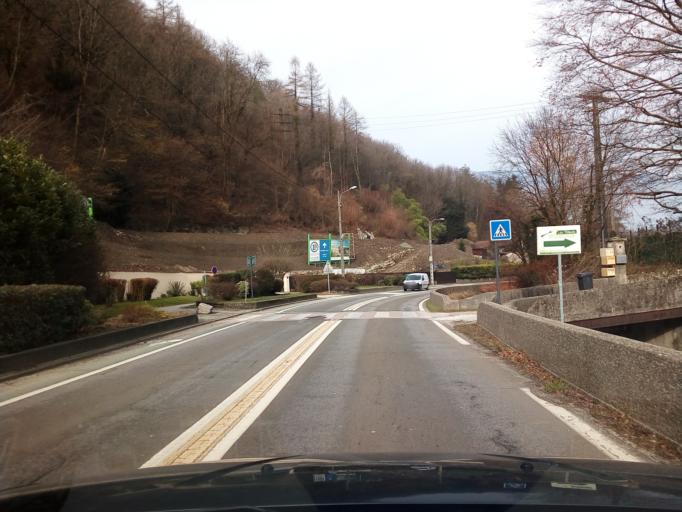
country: FR
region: Rhone-Alpes
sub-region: Departement de l'Isere
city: Gieres
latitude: 45.1756
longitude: 5.7898
